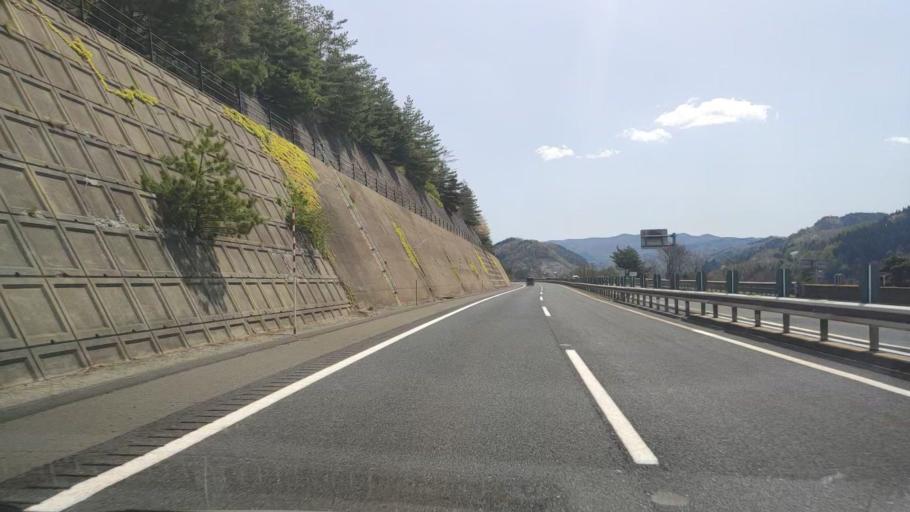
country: JP
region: Iwate
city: Ichinohe
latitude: 40.2310
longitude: 141.3130
